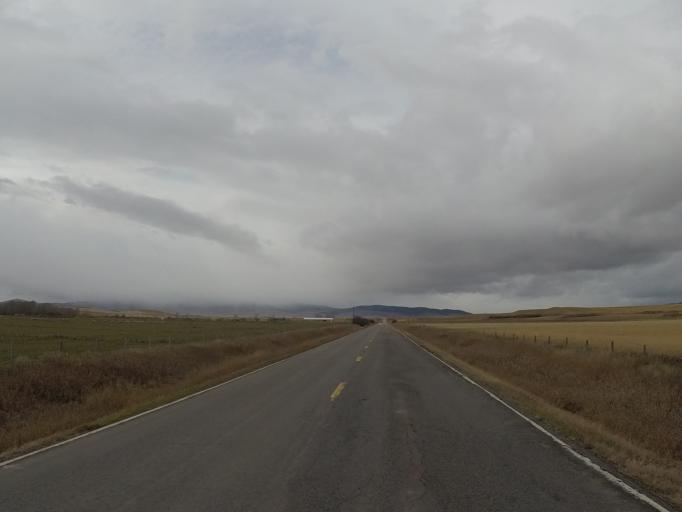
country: US
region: Montana
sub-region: Wheatland County
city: Harlowton
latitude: 46.4813
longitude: -110.2618
